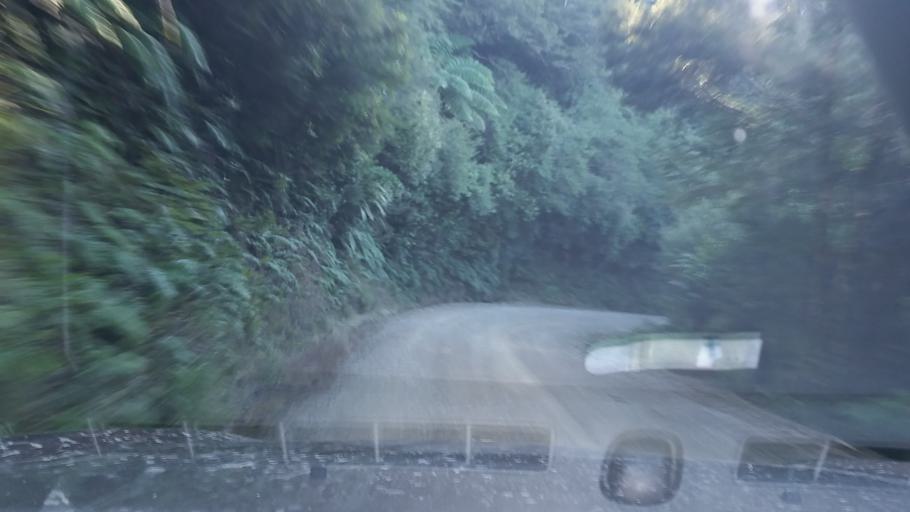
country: NZ
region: Marlborough
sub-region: Marlborough District
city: Picton
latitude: -41.0592
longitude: 174.1578
